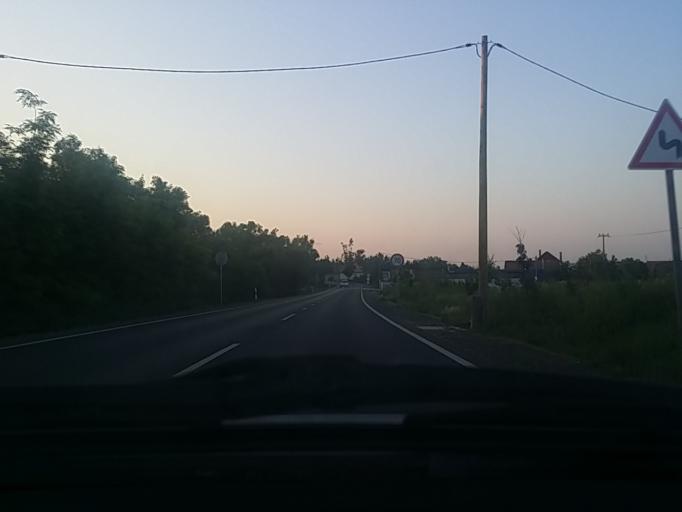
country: HU
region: Pest
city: Maglod
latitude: 47.4535
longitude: 19.3546
